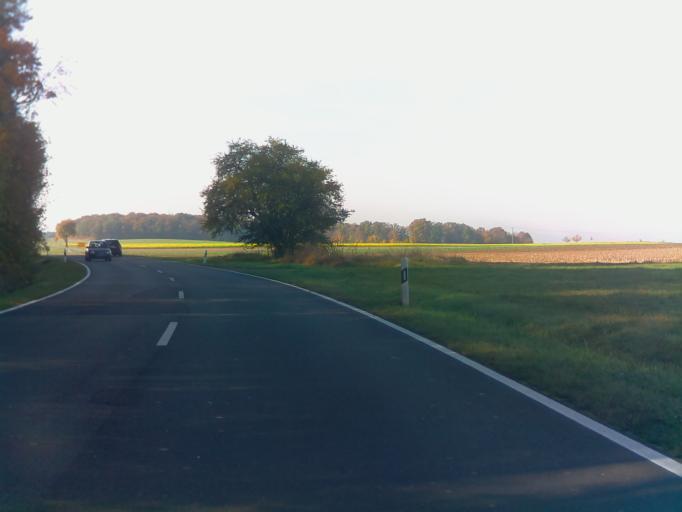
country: DE
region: Bavaria
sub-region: Regierungsbezirk Unterfranken
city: Oberschwarzach
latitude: 49.8495
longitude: 10.3958
